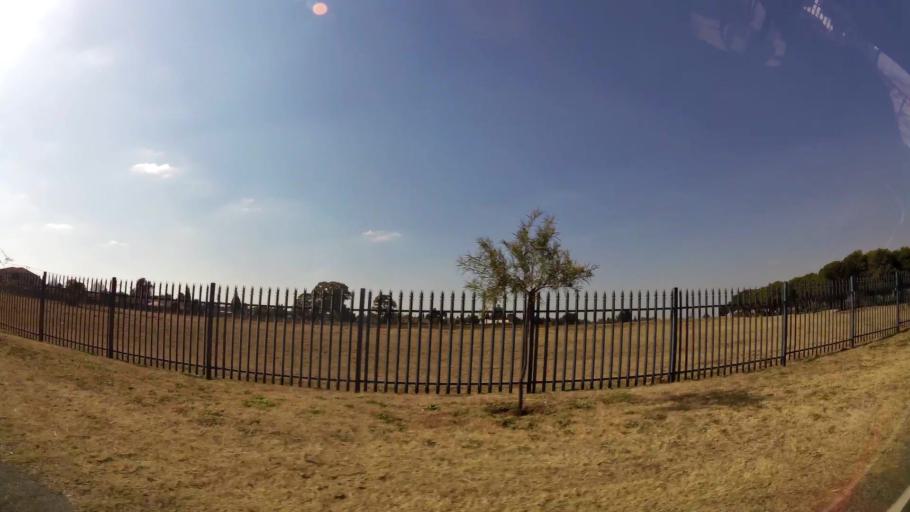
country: ZA
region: Gauteng
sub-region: West Rand District Municipality
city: Randfontein
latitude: -26.1560
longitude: 27.7016
